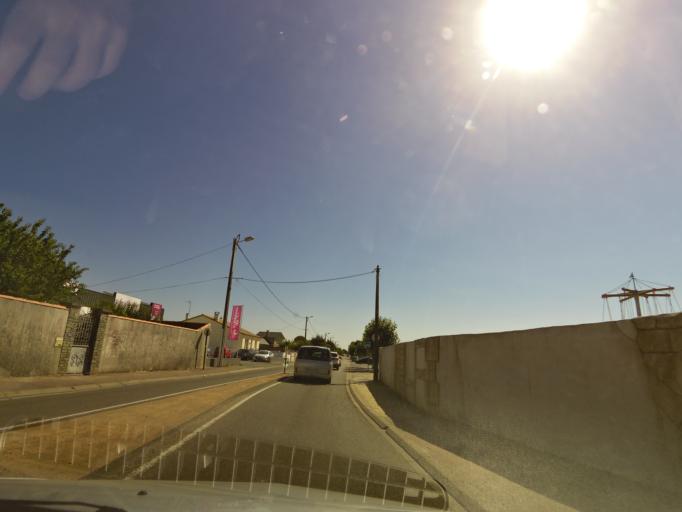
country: FR
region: Pays de la Loire
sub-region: Departement de la Vendee
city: Jard-sur-Mer
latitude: 46.4210
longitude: -1.5707
